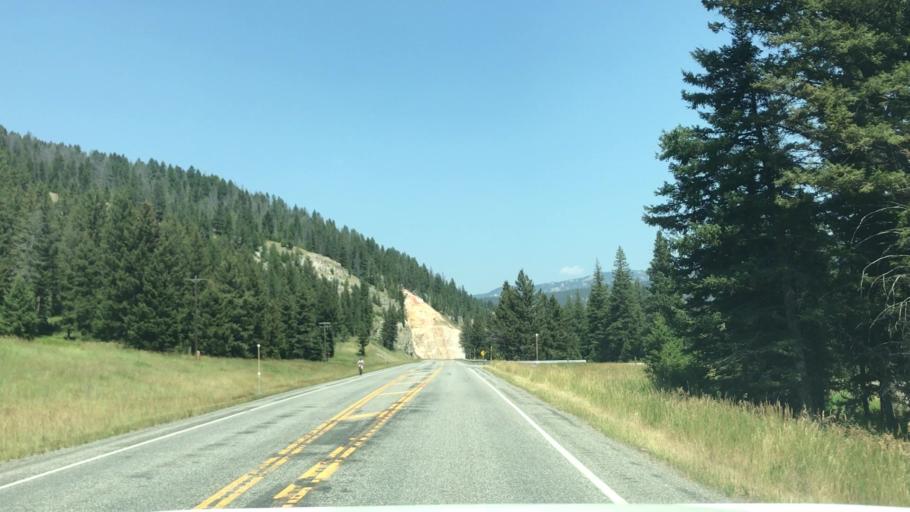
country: US
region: Montana
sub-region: Gallatin County
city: Big Sky
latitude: 45.1729
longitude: -111.2434
